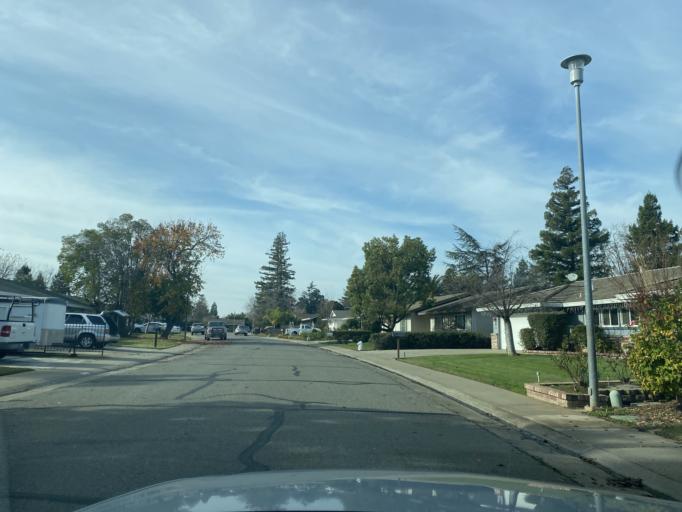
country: US
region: California
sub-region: Sacramento County
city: Elk Grove
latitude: 38.4073
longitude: -121.3796
